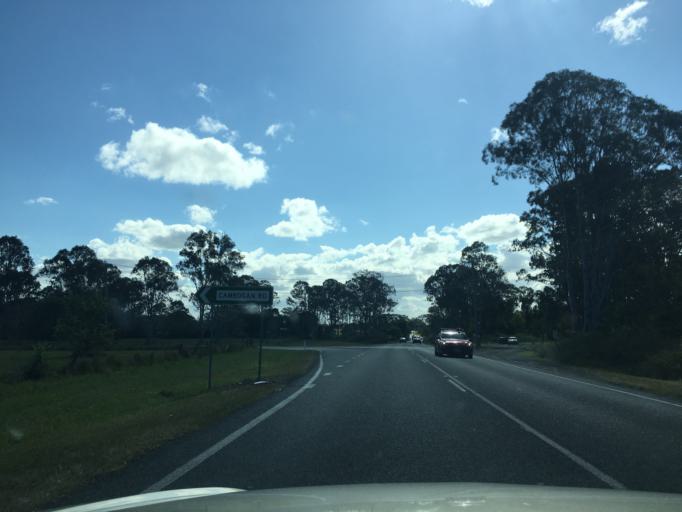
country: AU
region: Queensland
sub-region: Logan
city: Waterford West
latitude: -27.7090
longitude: 153.1419
